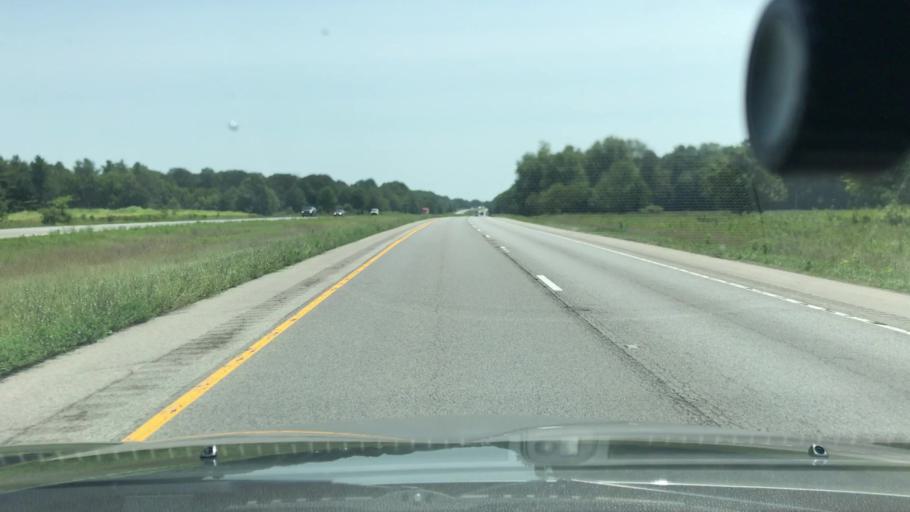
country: US
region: Illinois
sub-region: Clinton County
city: Wamac
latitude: 38.3840
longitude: -89.1226
